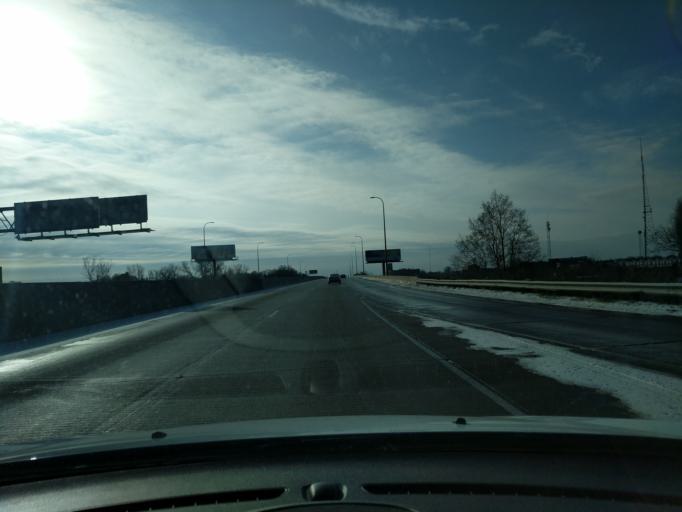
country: US
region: Minnesota
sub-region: Ramsey County
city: Lauderdale
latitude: 44.9755
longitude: -93.2025
